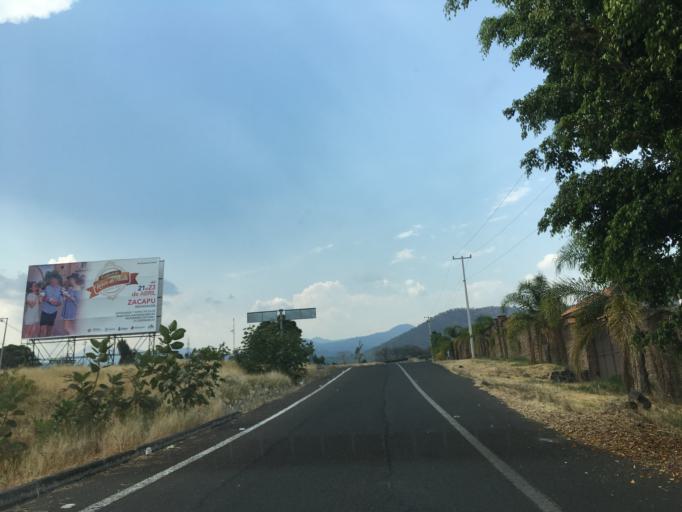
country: MX
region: Michoacan
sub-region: Ziracuaretiro
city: Patuan
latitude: 19.4225
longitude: -101.9222
